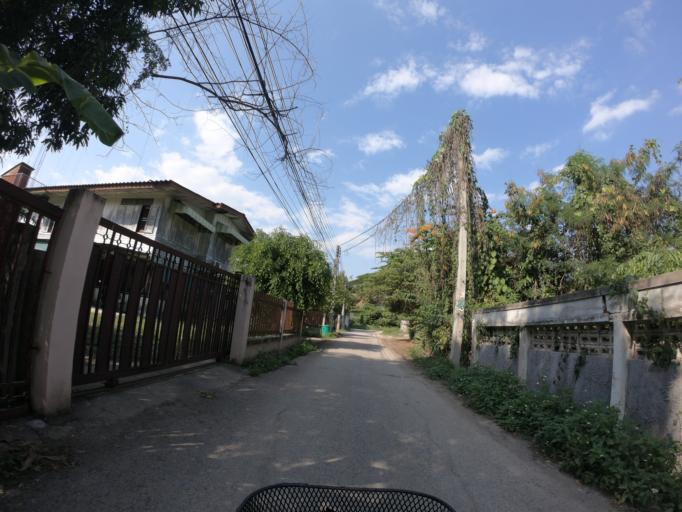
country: TH
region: Chiang Mai
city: Chiang Mai
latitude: 18.7941
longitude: 99.0152
